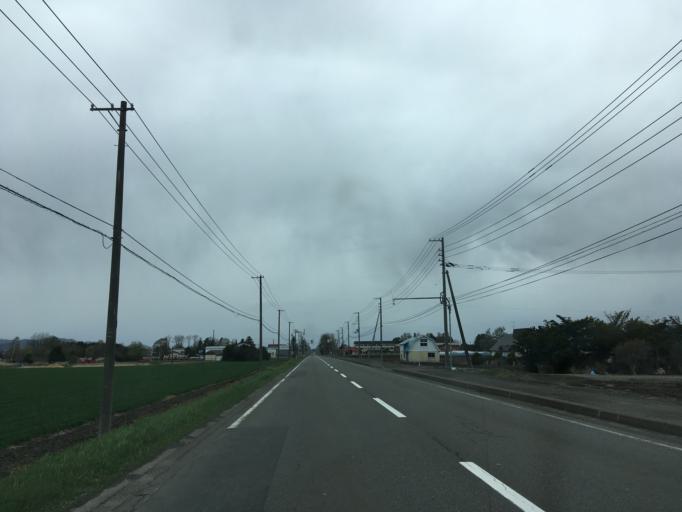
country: JP
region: Hokkaido
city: Chitose
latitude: 42.9364
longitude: 141.8056
